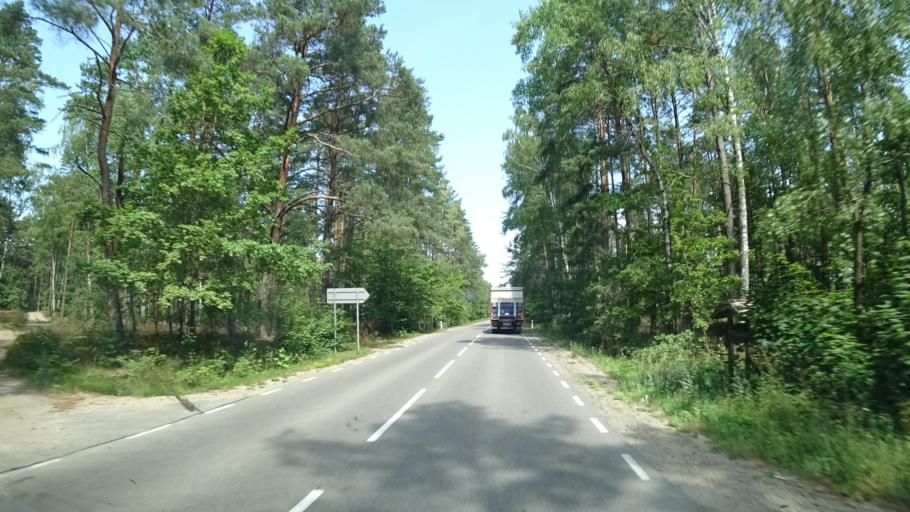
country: PL
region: Pomeranian Voivodeship
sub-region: Powiat koscierski
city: Lipusz
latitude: 54.0907
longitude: 17.8048
